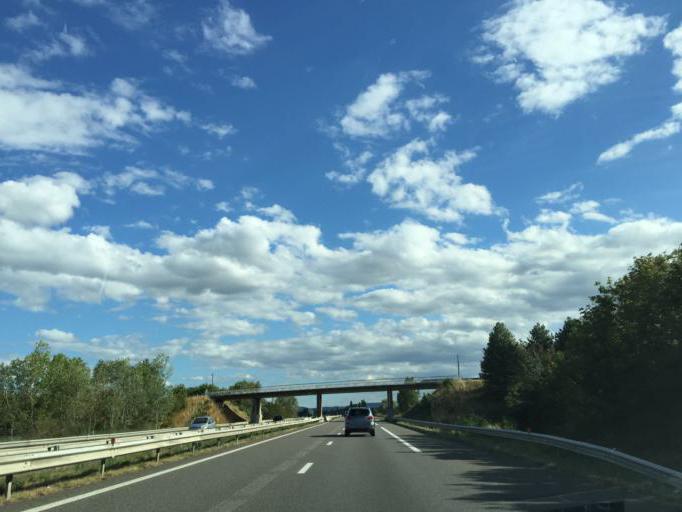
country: FR
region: Rhone-Alpes
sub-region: Departement de la Loire
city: Cuzieu
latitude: 45.5925
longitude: 4.2108
